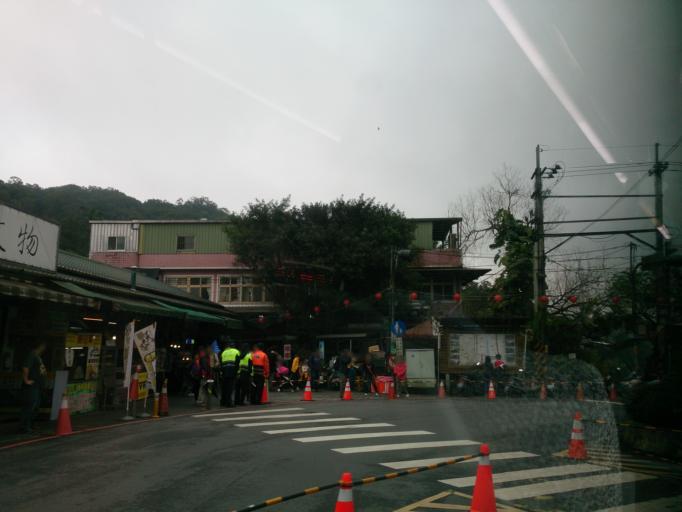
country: TW
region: Taiwan
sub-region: Keelung
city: Keelung
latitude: 25.0235
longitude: 121.7227
